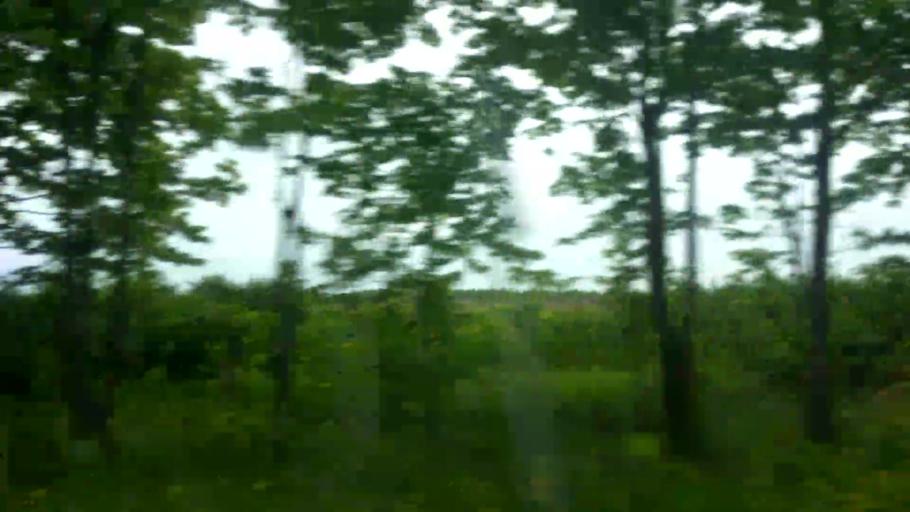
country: RU
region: Moskovskaya
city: Ozherel'ye
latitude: 54.8465
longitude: 38.2668
